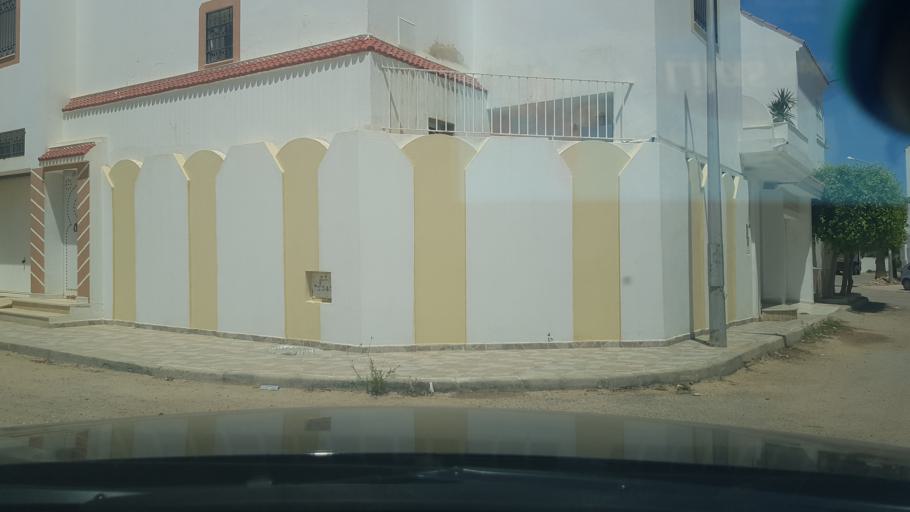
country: TN
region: Safaqis
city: Al Qarmadah
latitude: 34.8262
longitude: 10.7563
